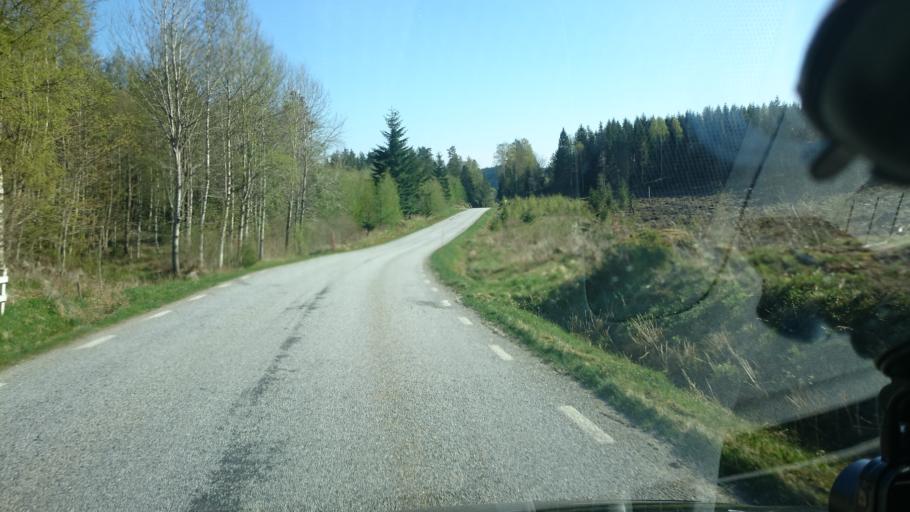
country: SE
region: Vaestra Goetaland
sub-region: Munkedals Kommun
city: Munkedal
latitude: 58.4191
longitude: 11.6865
